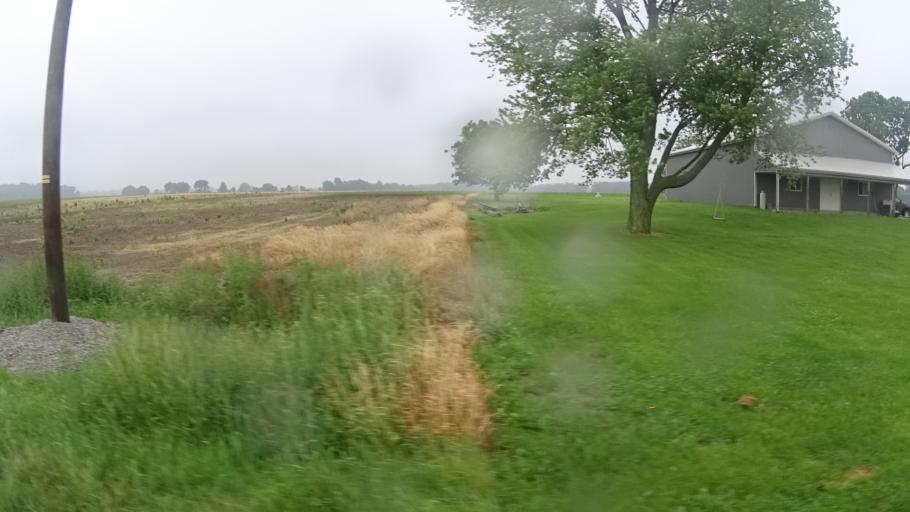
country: US
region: Ohio
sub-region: Huron County
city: Bellevue
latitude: 41.3533
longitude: -82.8442
